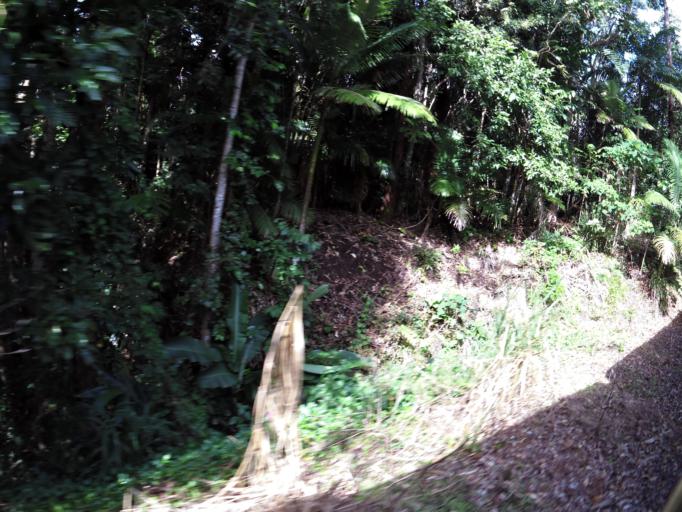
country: AU
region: Queensland
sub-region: Tablelands
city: Kuranda
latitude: -16.8300
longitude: 145.6382
